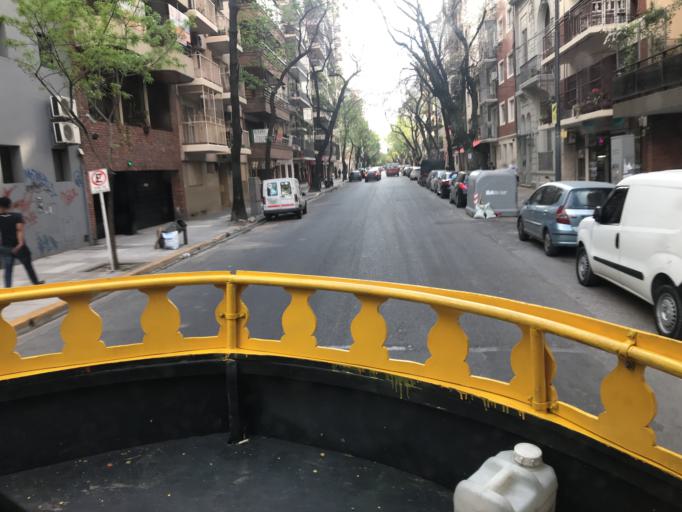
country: AR
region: Buenos Aires F.D.
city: Retiro
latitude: -34.5891
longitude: -58.4159
